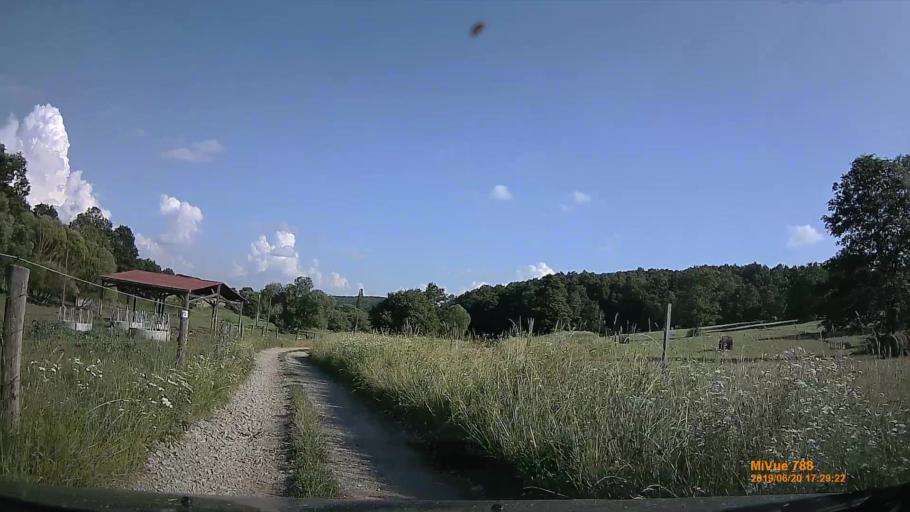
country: HU
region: Baranya
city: Buekkoesd
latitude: 46.1565
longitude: 18.0098
